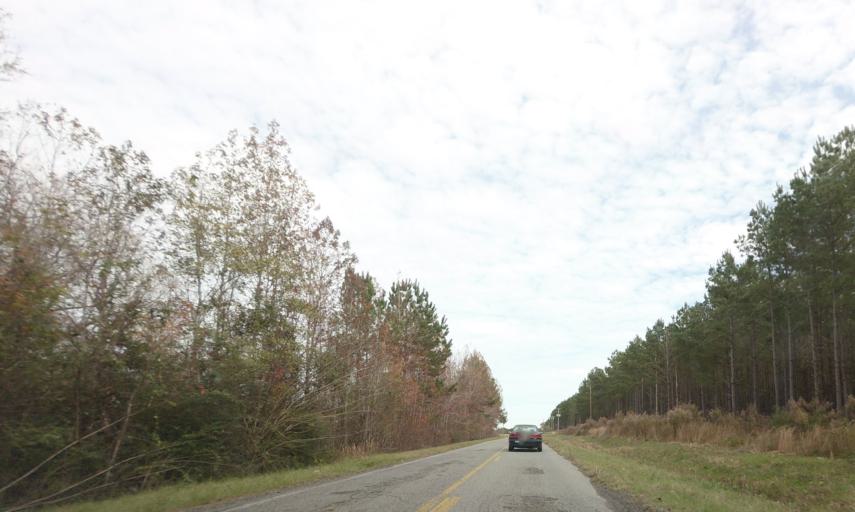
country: US
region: Georgia
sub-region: Dodge County
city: Chester
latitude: 32.4166
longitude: -83.1925
